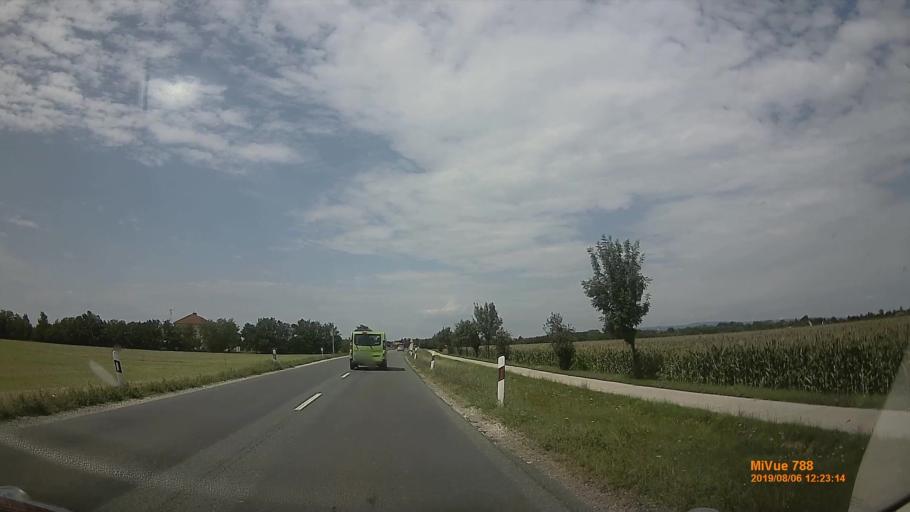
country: HU
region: Vas
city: Taplanszentkereszt
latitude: 47.1900
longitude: 16.7178
